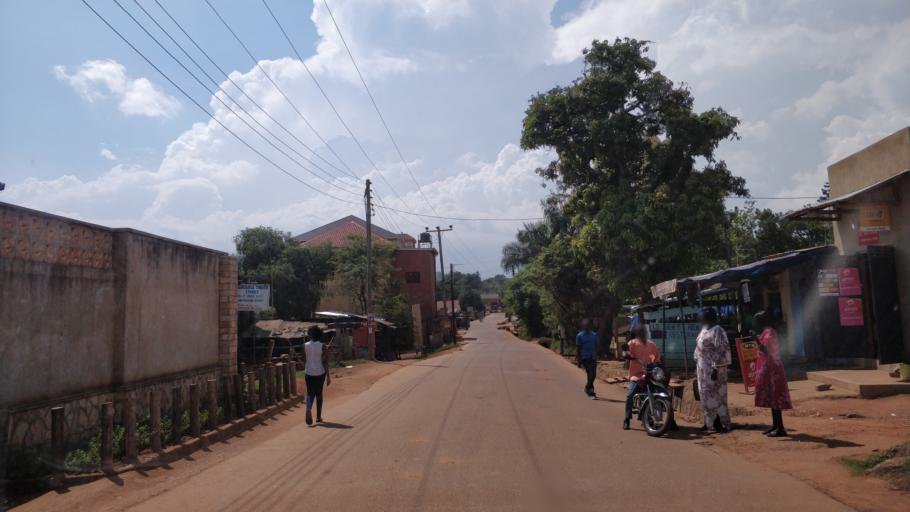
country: UG
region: Central Region
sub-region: Kampala District
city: Kampala
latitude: 0.2836
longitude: 32.6134
